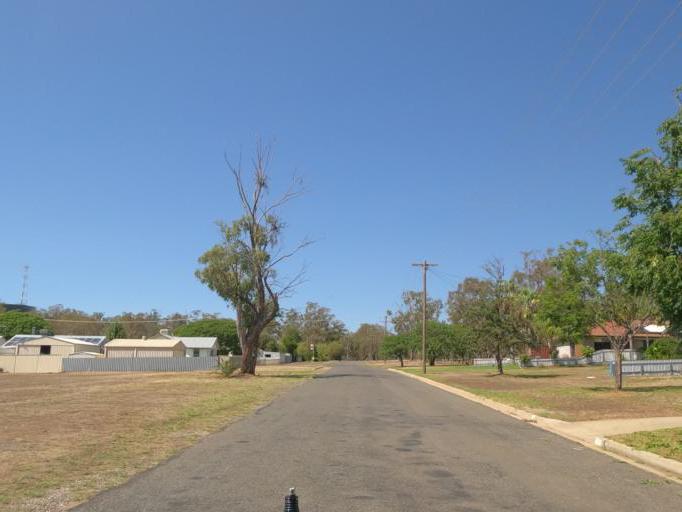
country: AU
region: New South Wales
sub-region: Corowa Shire
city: Mulwala
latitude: -35.9936
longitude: 145.9953
